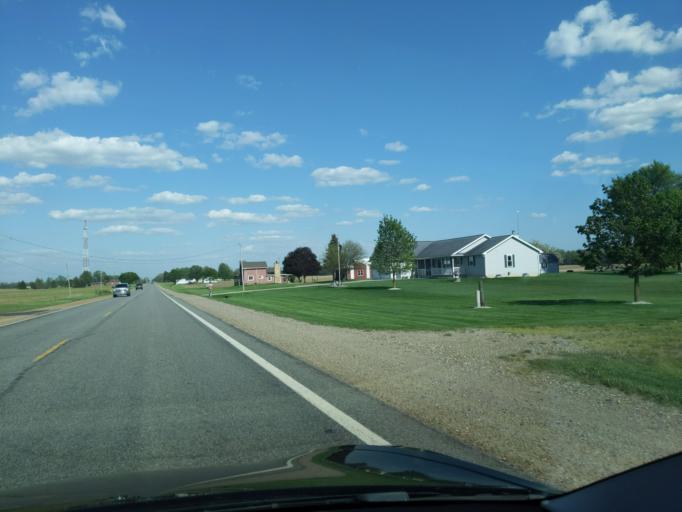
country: US
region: Michigan
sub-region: Ionia County
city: Portland
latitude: 42.7556
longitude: -84.9214
